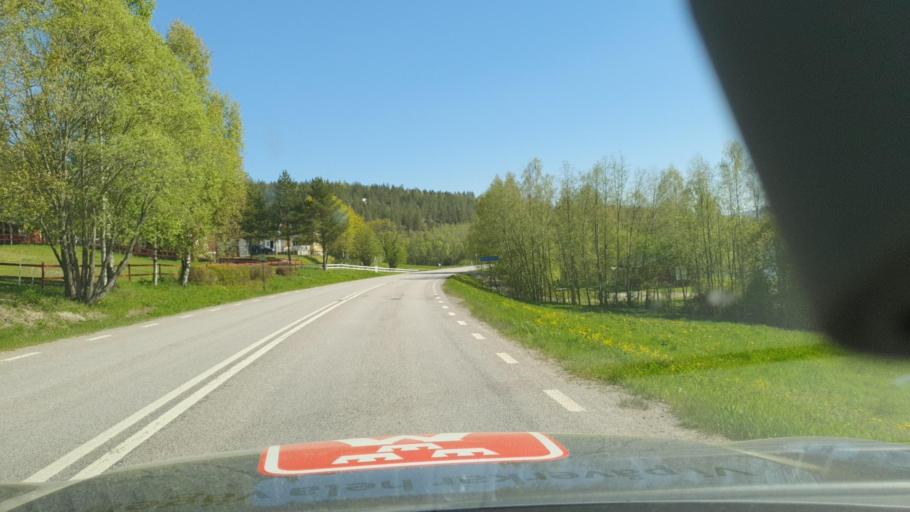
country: SE
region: Vaesternorrland
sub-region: OErnskoeldsviks Kommun
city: Ornskoldsvik
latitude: 63.3463
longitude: 18.6676
